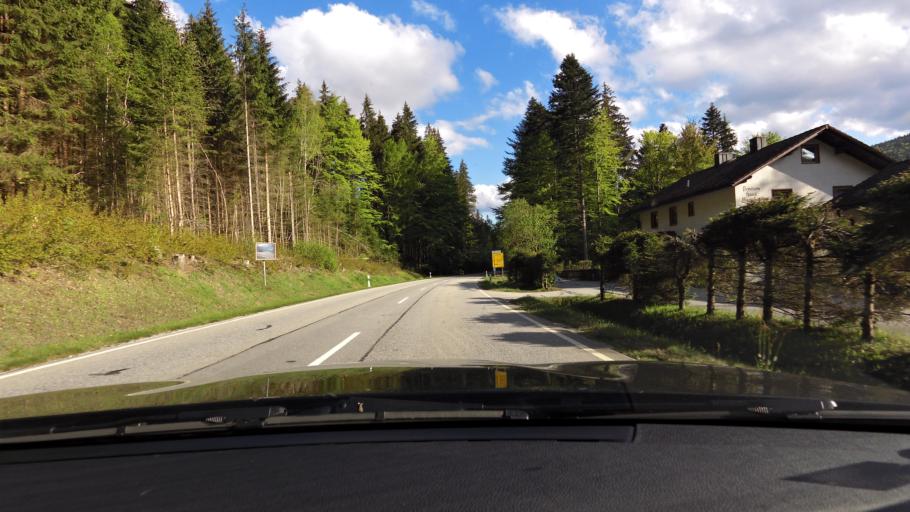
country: DE
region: Bavaria
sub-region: Lower Bavaria
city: Bayerisch Eisenstein
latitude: 49.0797
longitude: 13.2090
